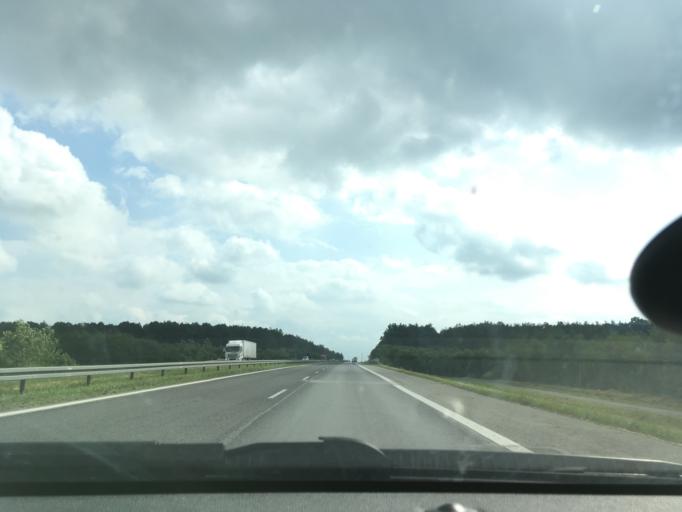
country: PL
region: Silesian Voivodeship
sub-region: Powiat czestochowski
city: Borowno
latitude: 50.9895
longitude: 19.2851
